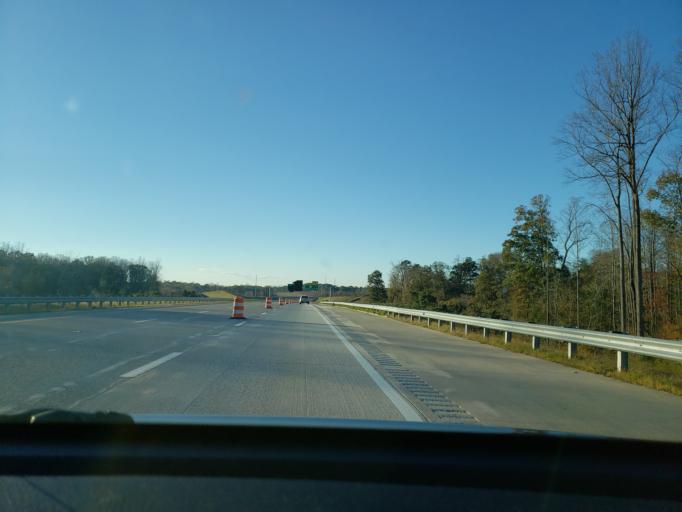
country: US
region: North Carolina
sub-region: Forsyth County
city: Walkertown
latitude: 36.1420
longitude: -80.1480
